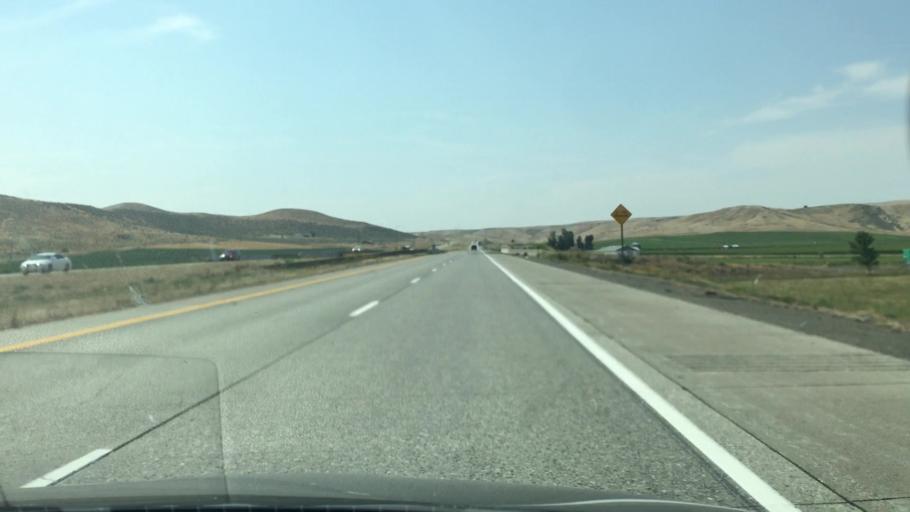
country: US
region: Idaho
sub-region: Elmore County
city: Glenns Ferry
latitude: 42.9612
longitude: -115.3066
